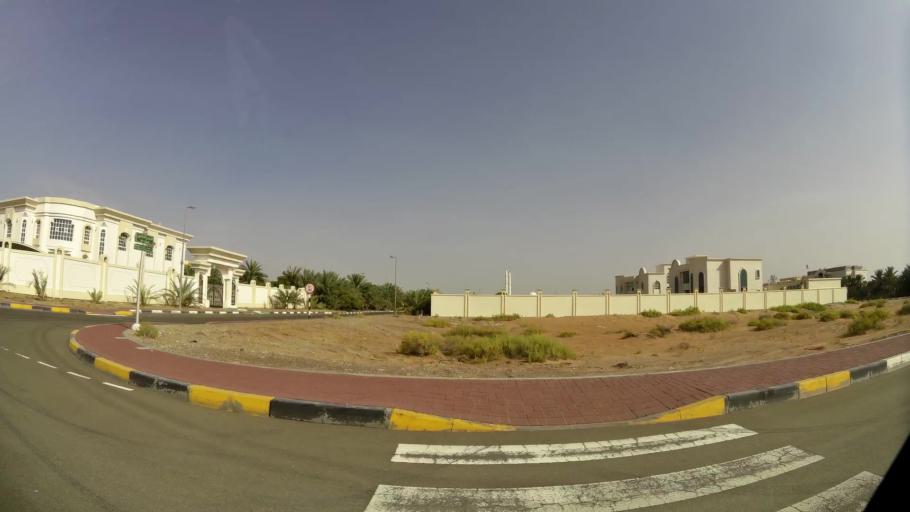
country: AE
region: Abu Dhabi
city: Al Ain
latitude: 24.2311
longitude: 55.6608
